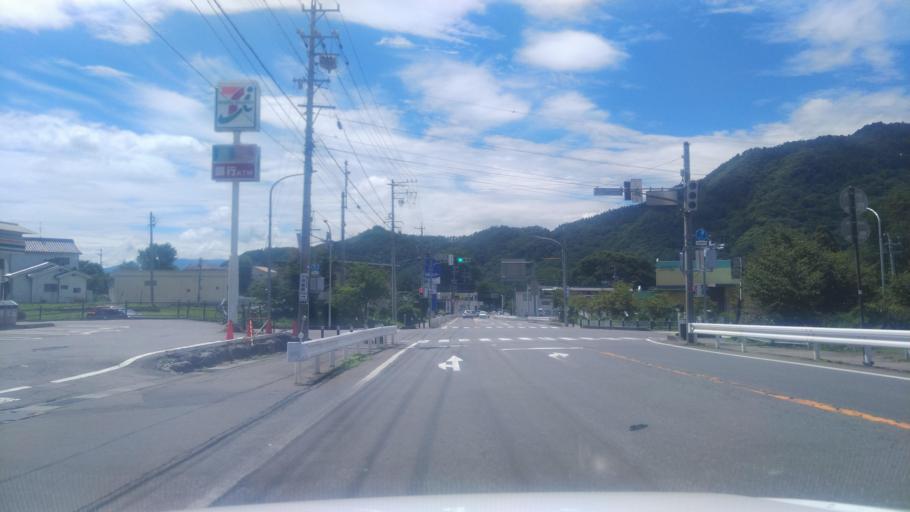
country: JP
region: Nagano
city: Ueda
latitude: 36.4388
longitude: 138.3052
